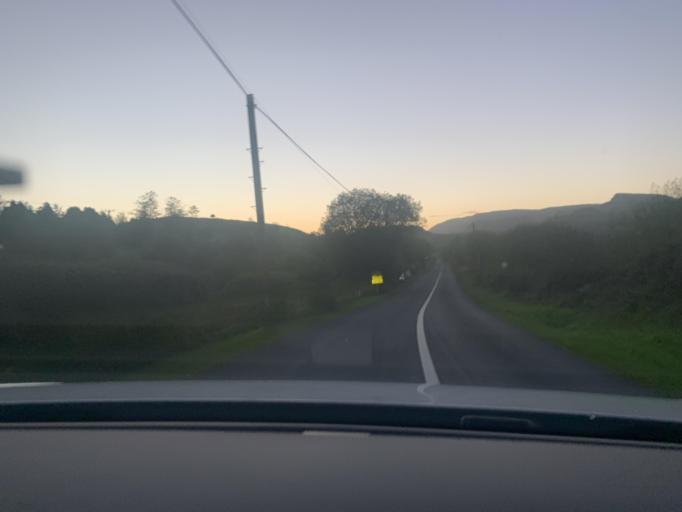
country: IE
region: Connaught
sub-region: County Leitrim
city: Manorhamilton
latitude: 54.2747
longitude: -8.2888
